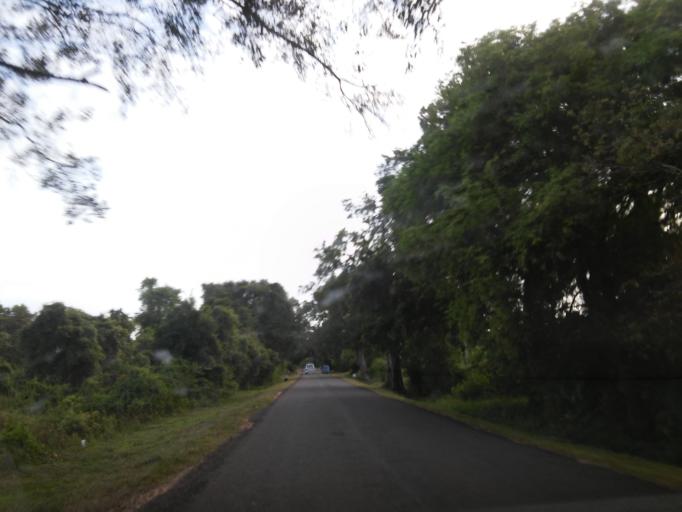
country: LK
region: Central
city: Sigiriya
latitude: 8.1087
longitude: 80.6325
